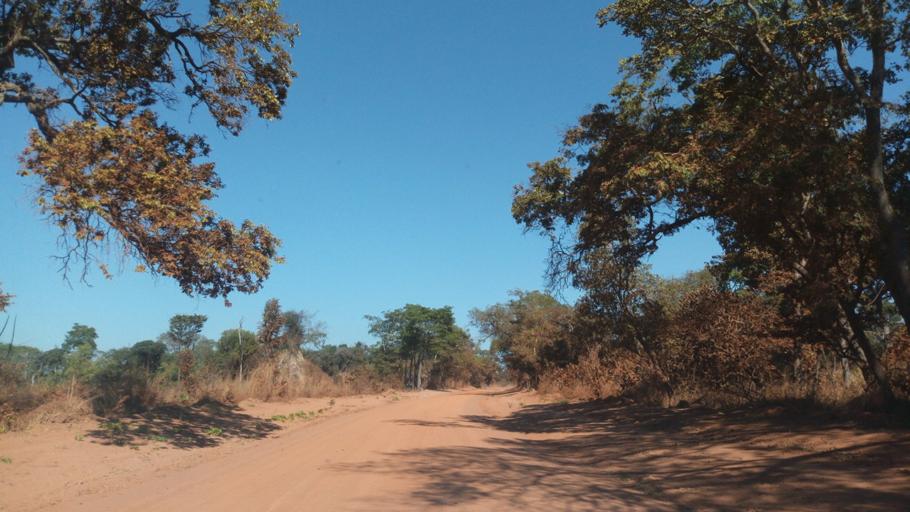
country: ZM
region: Luapula
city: Mwense
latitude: -10.7375
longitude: 28.3374
